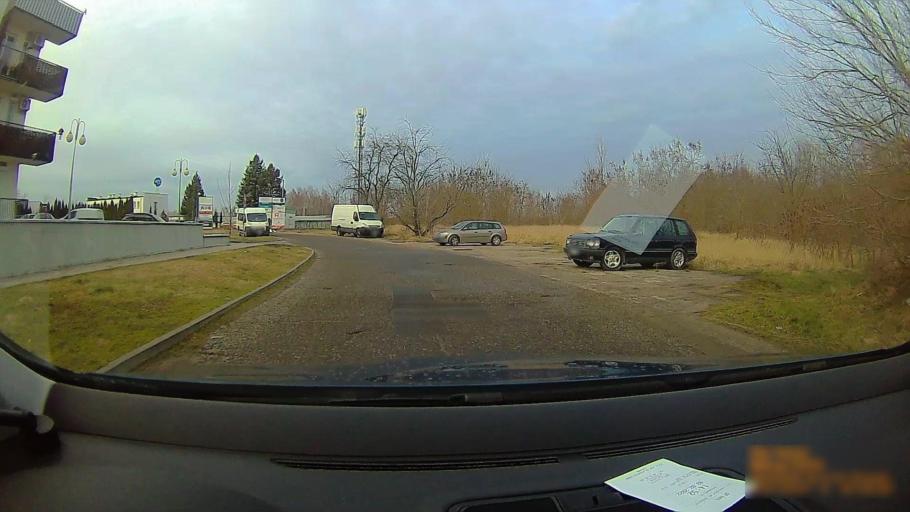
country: PL
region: Greater Poland Voivodeship
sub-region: Konin
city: Konin
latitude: 52.2356
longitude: 18.2183
